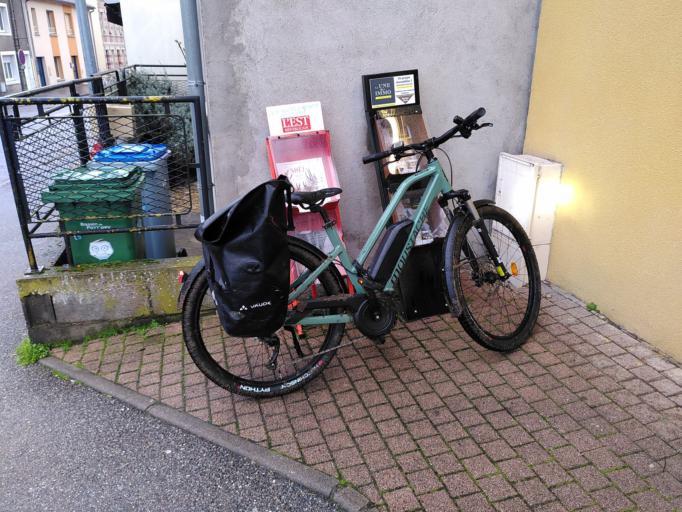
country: FR
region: Lorraine
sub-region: Departement de Meurthe-et-Moselle
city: Liverdun
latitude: 48.7497
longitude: 6.0662
